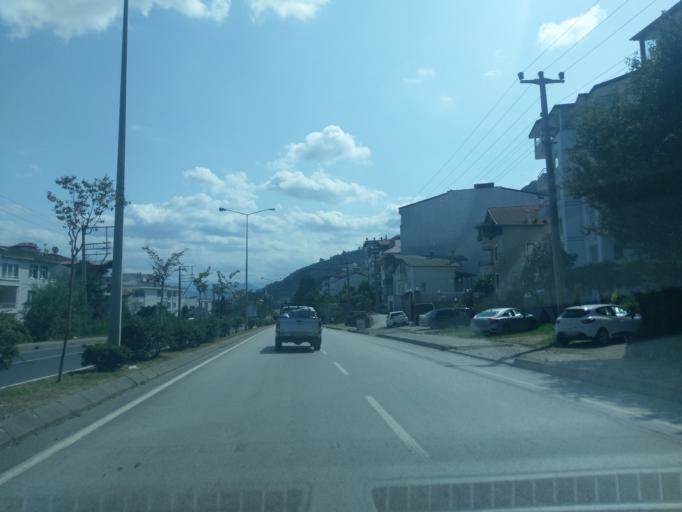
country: TR
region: Ordu
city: Ordu
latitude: 41.0087
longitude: 37.8687
